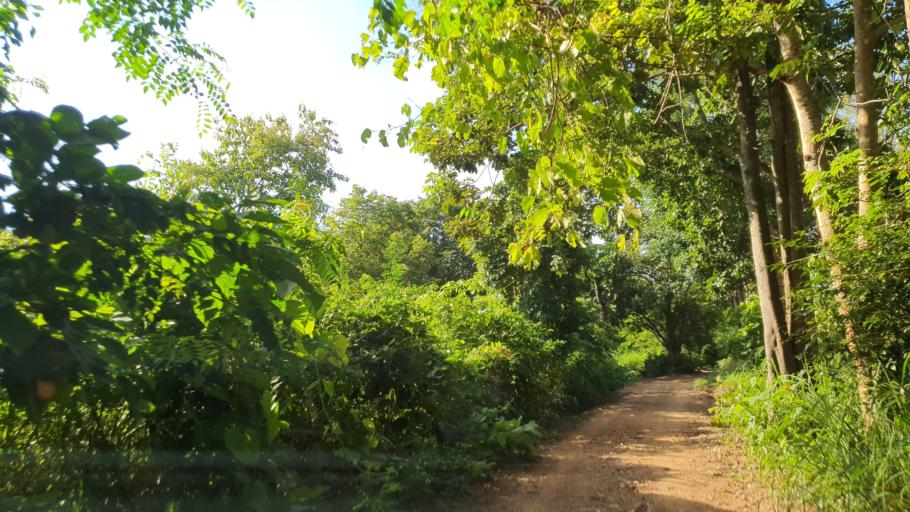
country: TH
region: Chiang Mai
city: Hang Dong
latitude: 18.7190
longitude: 98.8531
